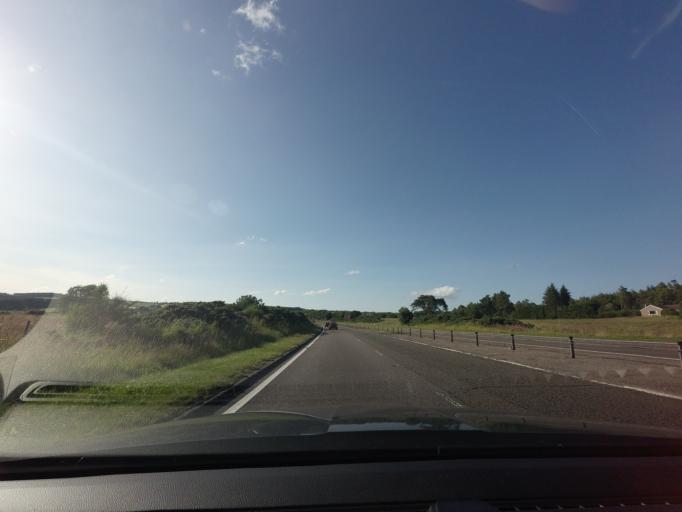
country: GB
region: Scotland
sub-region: Highland
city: Conon Bridge
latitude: 57.5358
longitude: -4.3302
